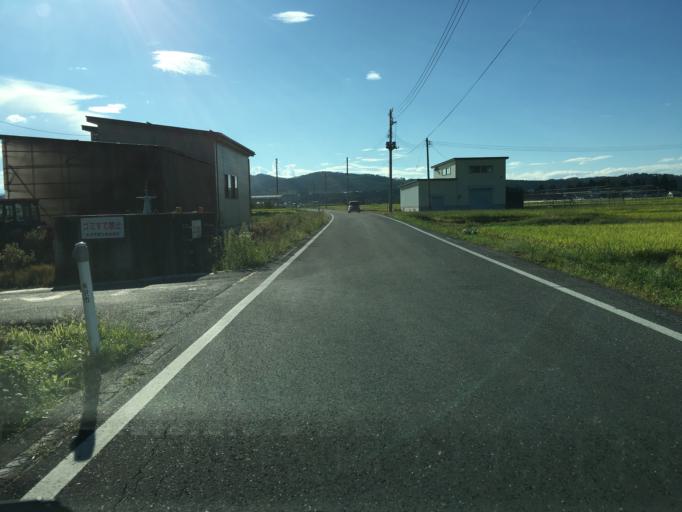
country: JP
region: Yamagata
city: Yonezawa
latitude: 37.9255
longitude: 140.0957
